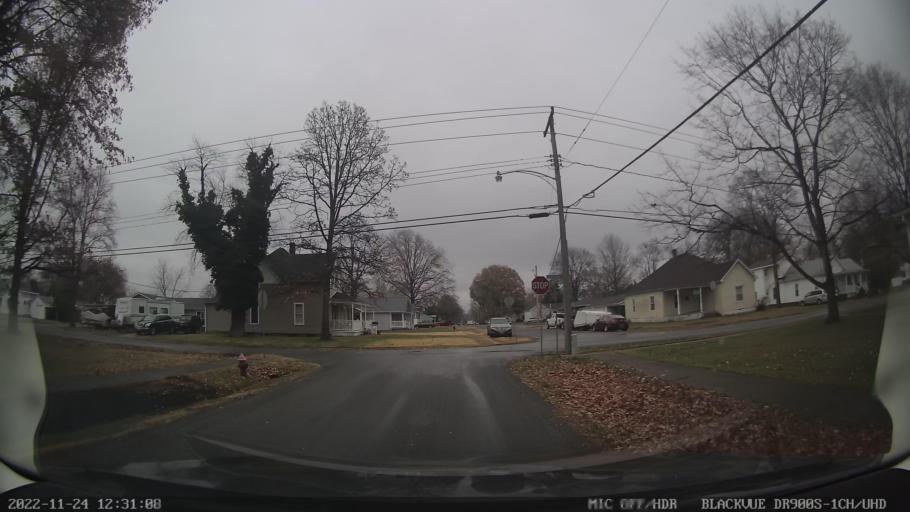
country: US
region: Illinois
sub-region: Macoupin County
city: Staunton
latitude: 39.0160
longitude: -89.7821
